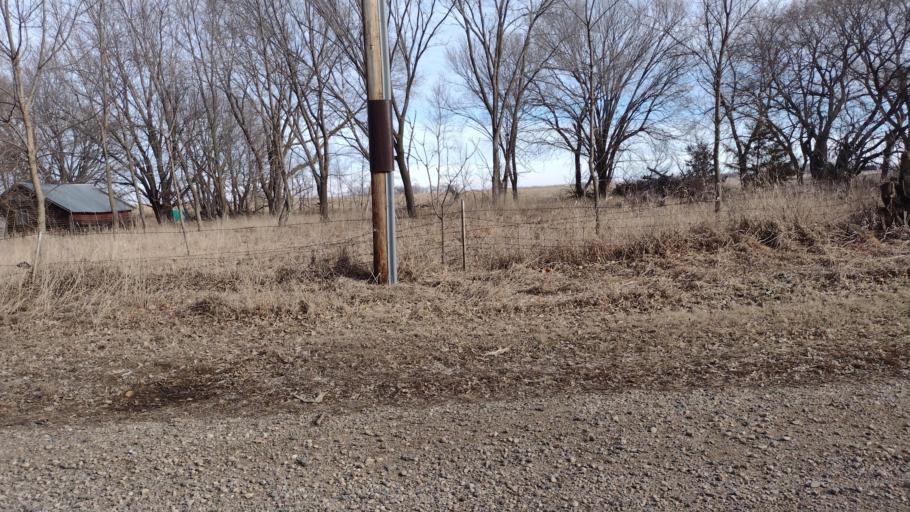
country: US
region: South Dakota
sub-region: Union County
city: Beresford
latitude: 42.9622
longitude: -96.8055
